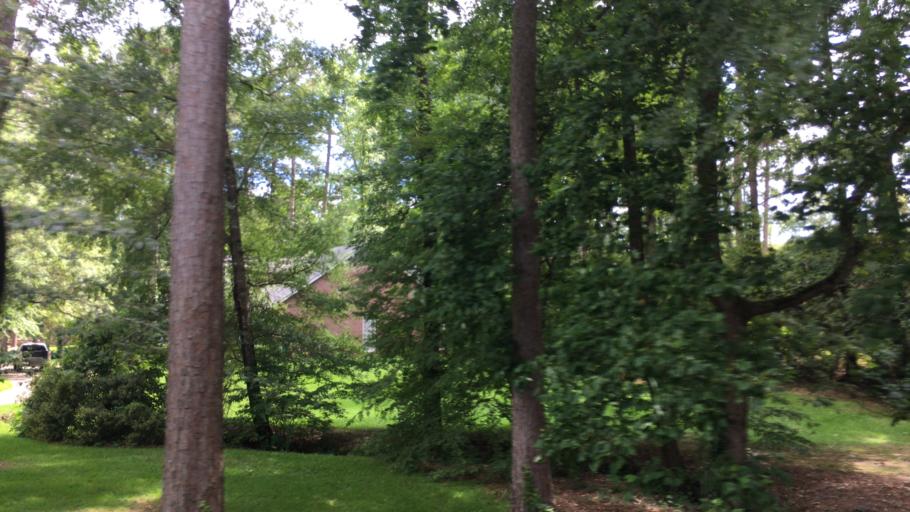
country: US
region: Louisiana
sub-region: Lincoln Parish
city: Ruston
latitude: 32.5502
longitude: -92.6321
